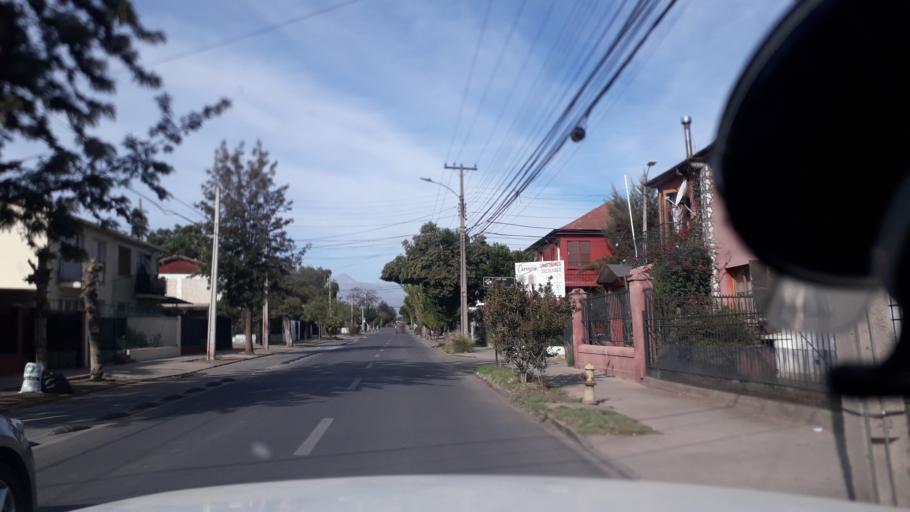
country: CL
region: Valparaiso
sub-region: Provincia de San Felipe
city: San Felipe
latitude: -32.7521
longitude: -70.7174
